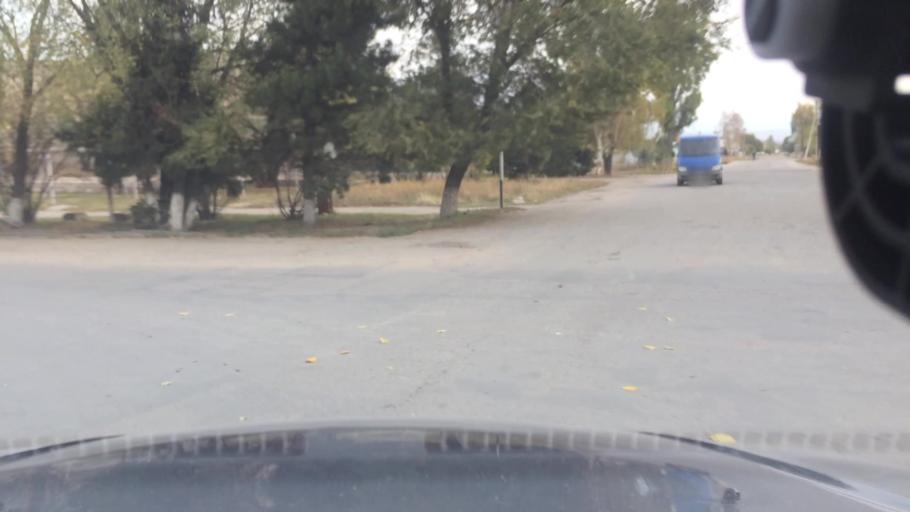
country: KG
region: Ysyk-Koel
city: Karakol
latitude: 42.4958
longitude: 78.3918
